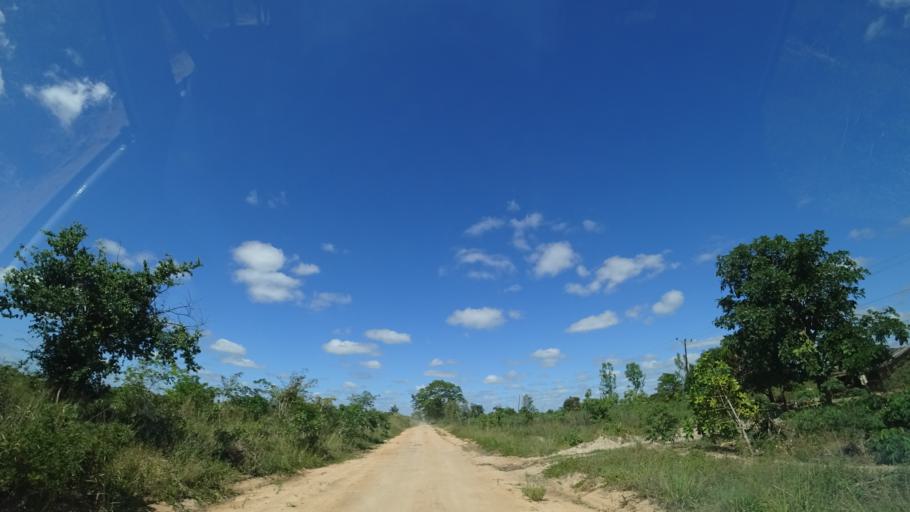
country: MZ
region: Sofala
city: Dondo
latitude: -19.2849
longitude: 34.6859
